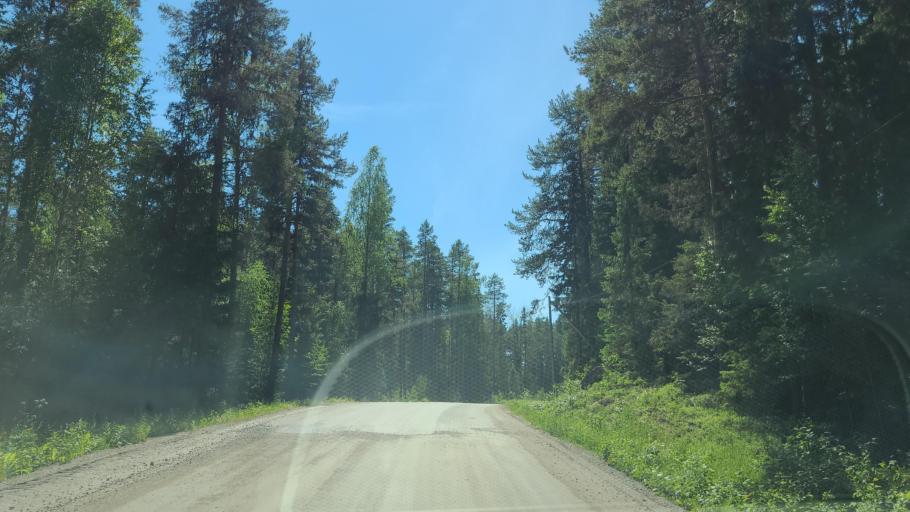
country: SE
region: Vaesterbotten
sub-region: Bjurholms Kommun
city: Bjurholm
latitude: 63.6980
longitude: 18.8962
